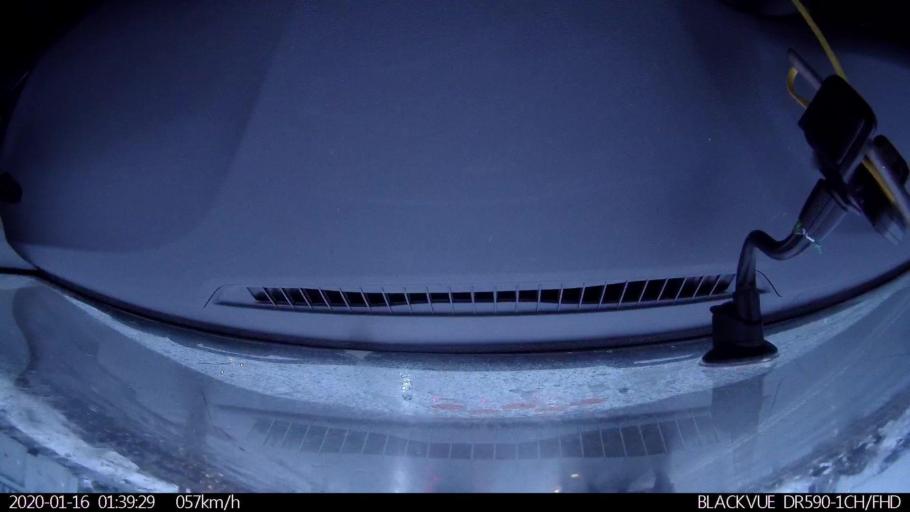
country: RU
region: Nizjnij Novgorod
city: Gorbatovka
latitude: 56.3341
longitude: 43.7950
